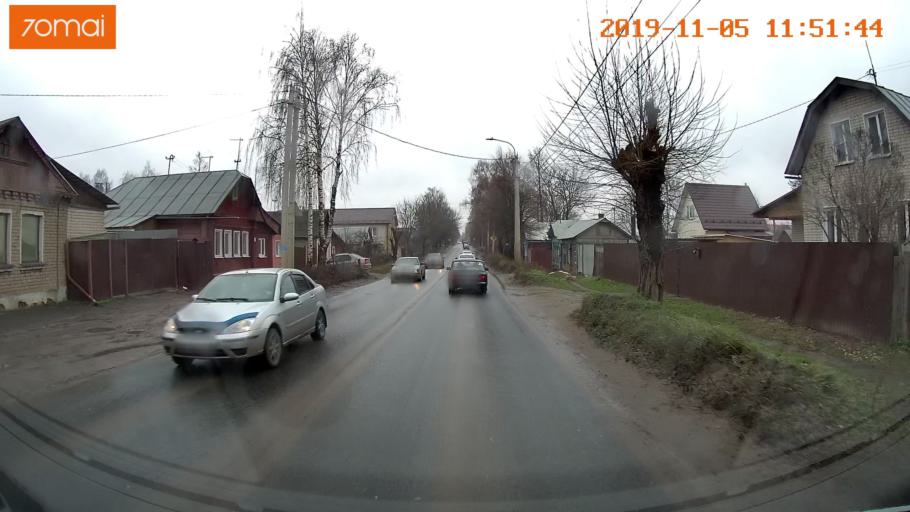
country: RU
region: Ivanovo
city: Bogorodskoye
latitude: 57.0041
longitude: 41.0287
